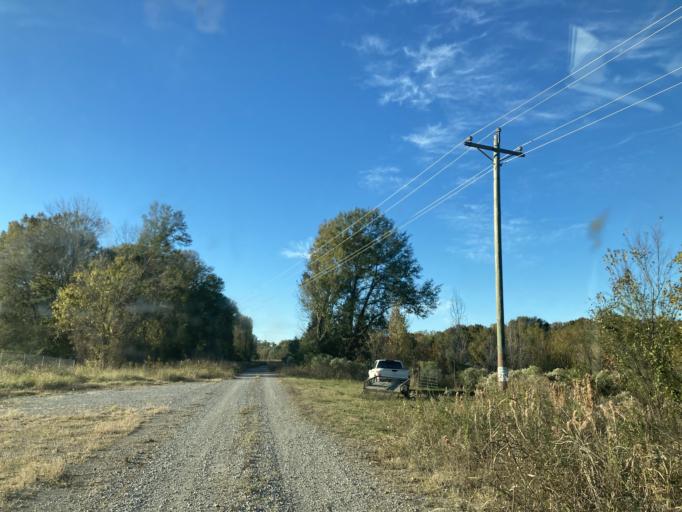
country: US
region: Mississippi
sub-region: Yazoo County
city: Yazoo City
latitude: 32.8922
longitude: -90.4313
